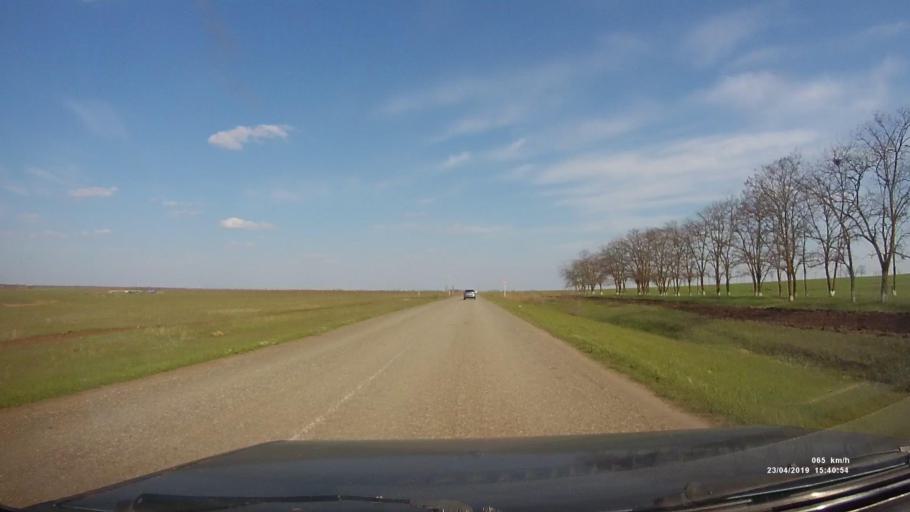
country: RU
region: Rostov
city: Remontnoye
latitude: 46.5533
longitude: 43.0435
